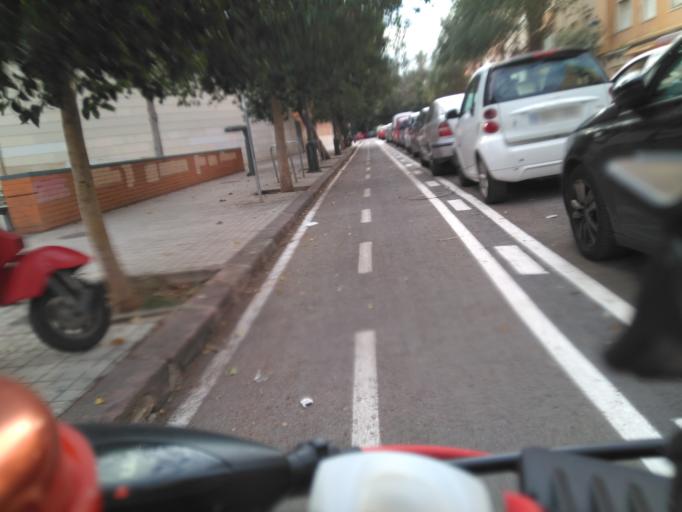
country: ES
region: Valencia
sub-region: Provincia de Valencia
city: Valencia
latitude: 39.4830
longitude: -0.3698
